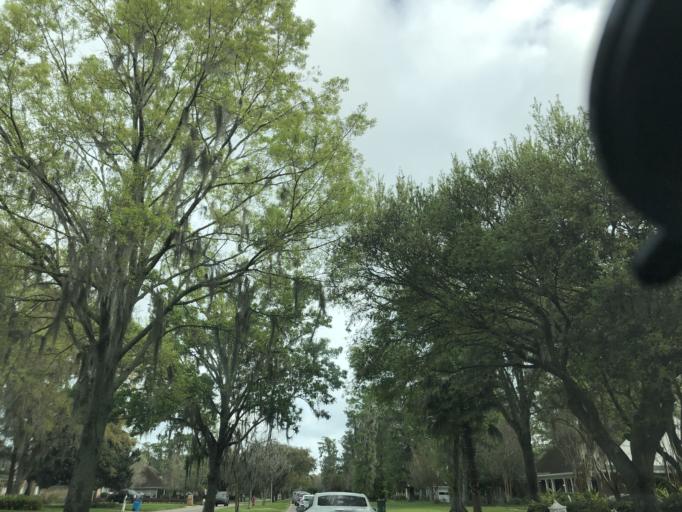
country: US
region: Louisiana
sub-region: Saint Charles Parish
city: New Sarpy
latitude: 29.9756
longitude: -90.3646
